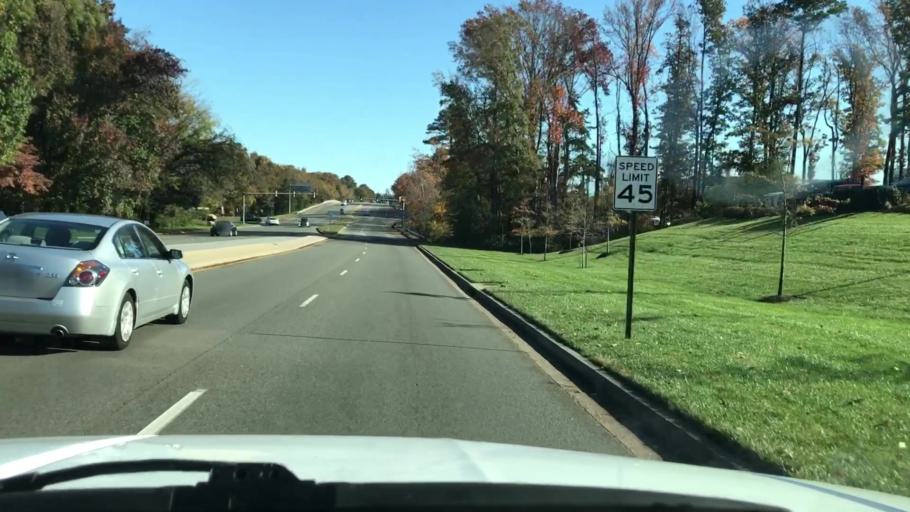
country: US
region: Virginia
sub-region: Henrico County
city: Tuckahoe
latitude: 37.6037
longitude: -77.5256
